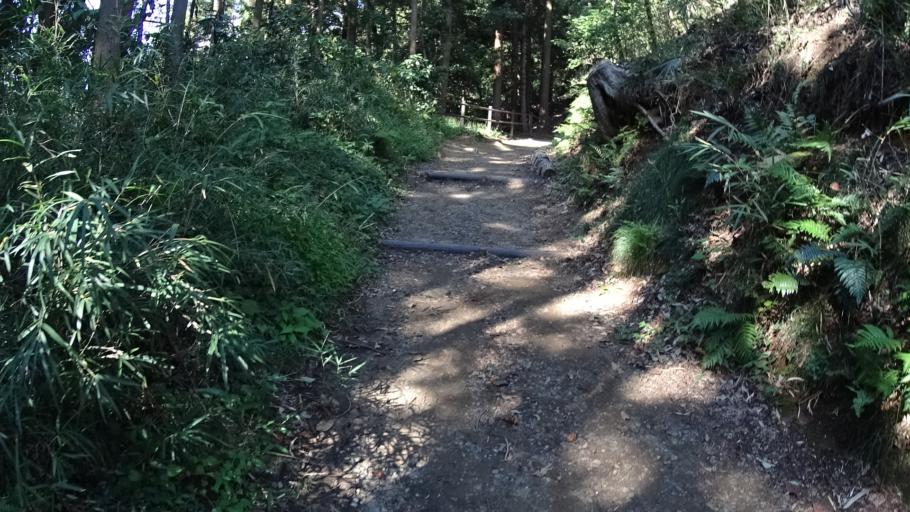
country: JP
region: Kanagawa
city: Kamakura
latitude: 35.3601
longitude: 139.5925
